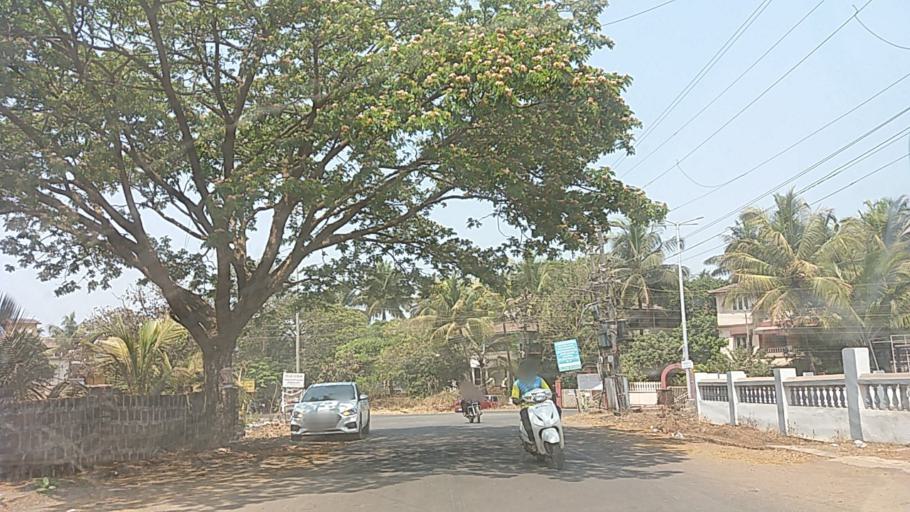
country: IN
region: Goa
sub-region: North Goa
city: Panaji
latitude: 15.5183
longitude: 73.8331
